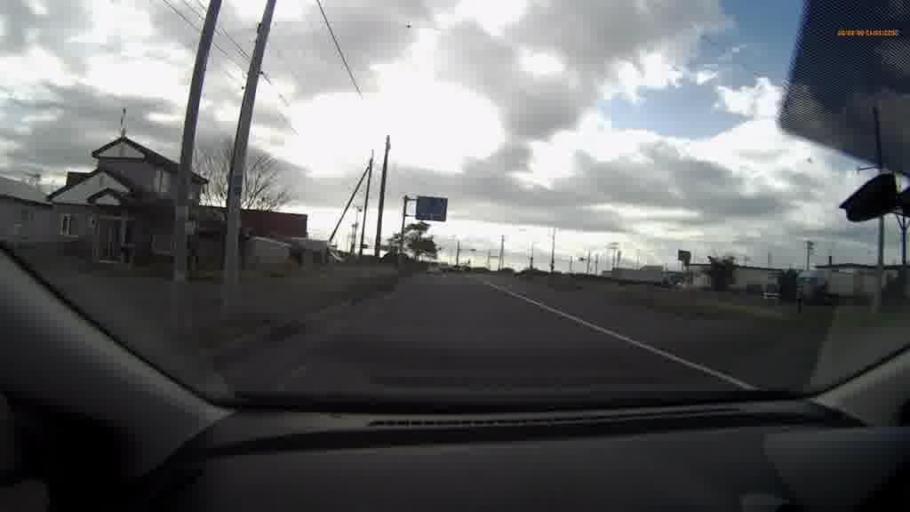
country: JP
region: Hokkaido
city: Kushiro
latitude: 43.0129
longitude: 144.2652
